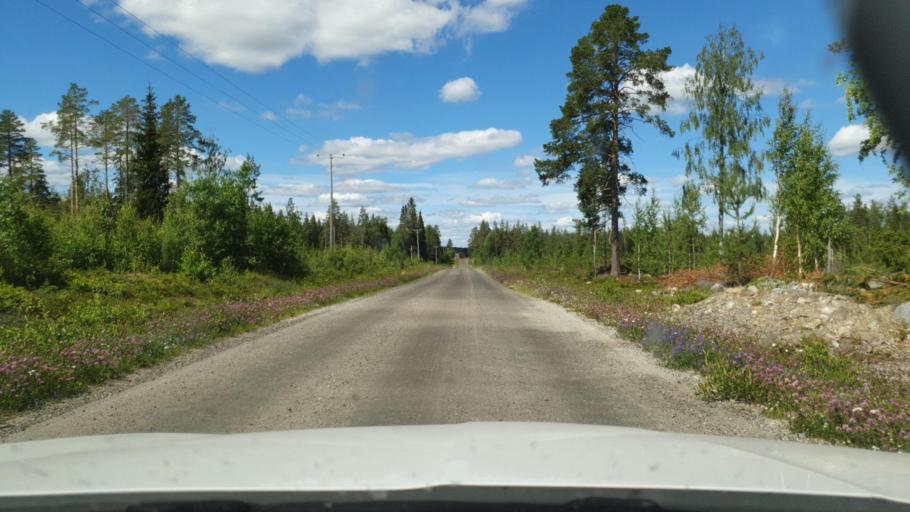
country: SE
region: Vaesterbotten
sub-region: Skelleftea Kommun
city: Backa
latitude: 65.1782
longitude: 21.0809
